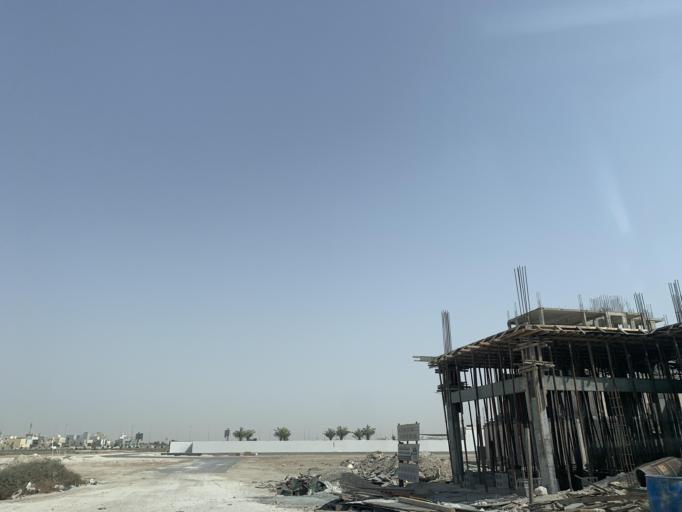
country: BH
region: Manama
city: Jidd Hafs
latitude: 26.2100
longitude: 50.5133
